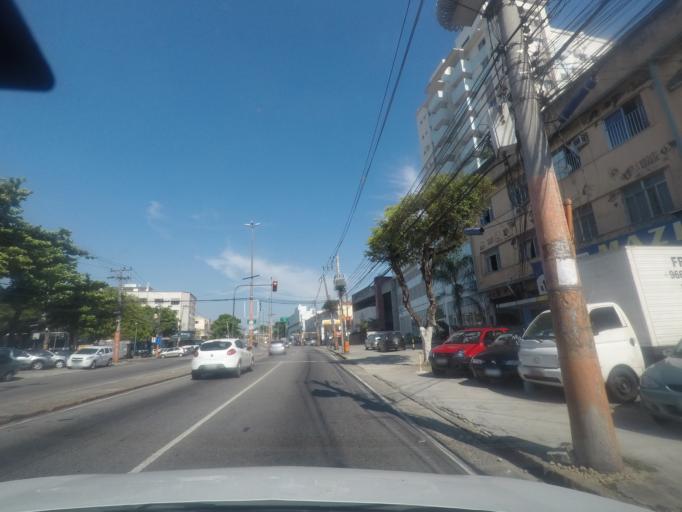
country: BR
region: Rio de Janeiro
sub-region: Sao Joao De Meriti
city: Sao Joao de Meriti
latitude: -22.8828
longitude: -43.3454
